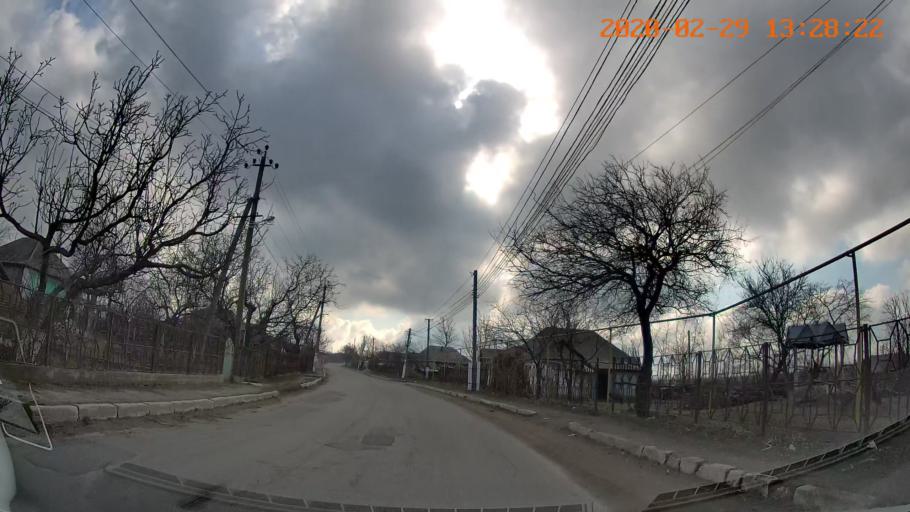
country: MD
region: Telenesti
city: Camenca
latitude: 47.9061
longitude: 28.6424
